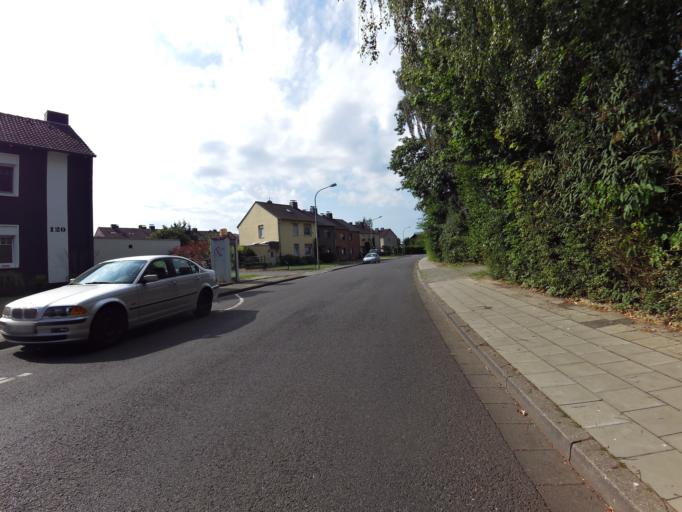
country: DE
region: North Rhine-Westphalia
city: Baesweiler
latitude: 50.9222
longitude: 6.2107
